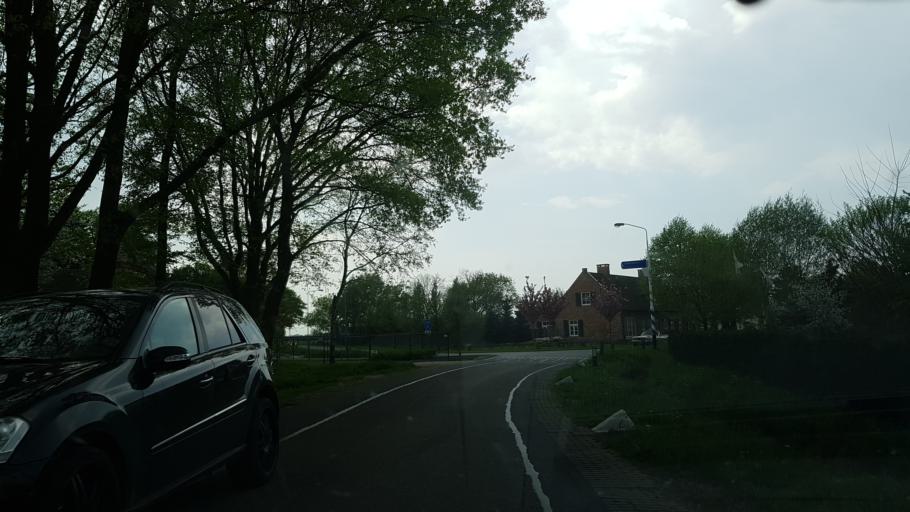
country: NL
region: Limburg
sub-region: Gemeente Nederweert
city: Nederweert
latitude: 51.2883
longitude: 5.7347
